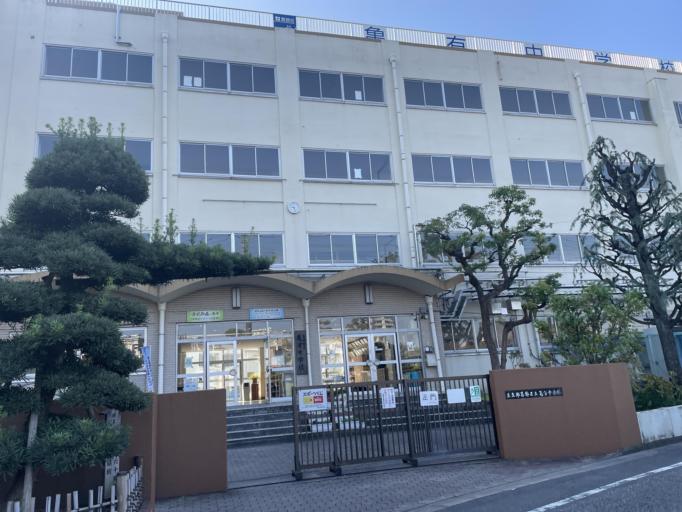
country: JP
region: Chiba
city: Matsudo
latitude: 35.7604
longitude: 139.8469
